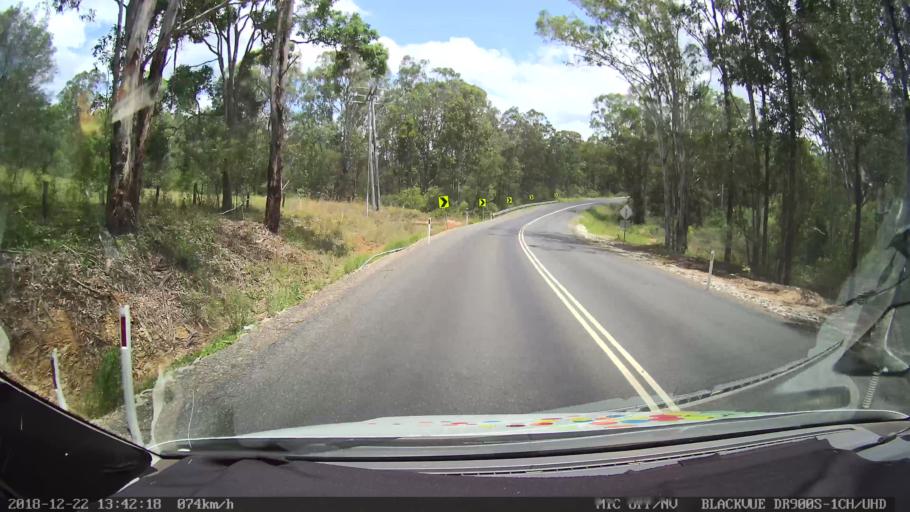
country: AU
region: New South Wales
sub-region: Clarence Valley
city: Coutts Crossing
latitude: -29.9220
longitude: 152.7544
